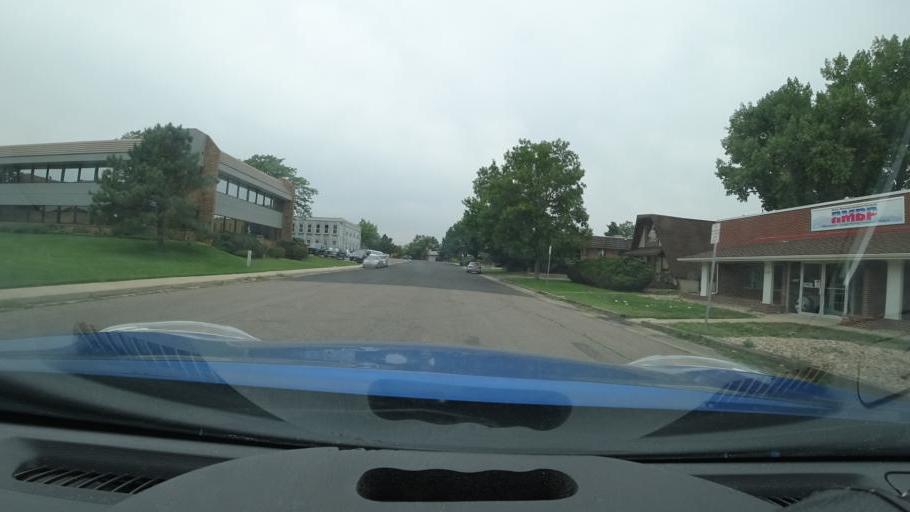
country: US
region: Colorado
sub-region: Arapahoe County
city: Glendale
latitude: 39.6797
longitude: -104.9067
